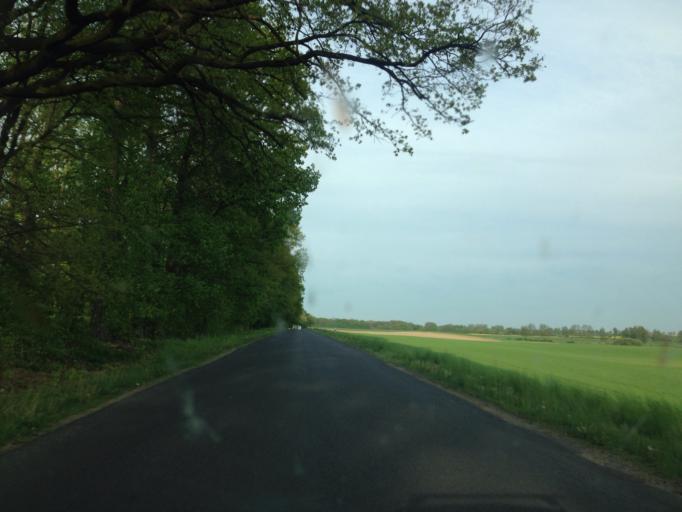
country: PL
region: Kujawsko-Pomorskie
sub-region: Powiat wabrzeski
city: Debowa Laka
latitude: 53.2586
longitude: 19.0617
